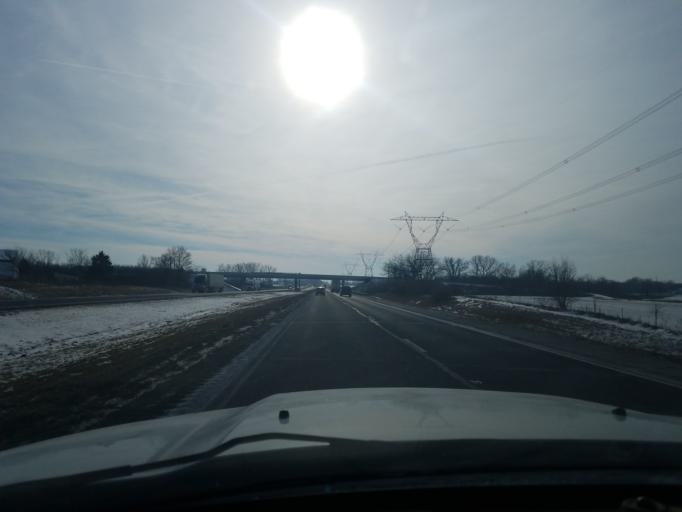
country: US
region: Indiana
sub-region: Huntington County
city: Roanoke
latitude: 40.9331
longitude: -85.3127
